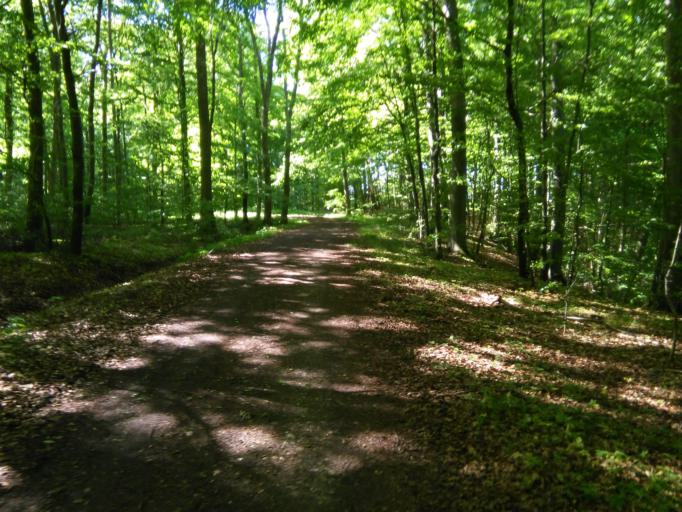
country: DK
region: Central Jutland
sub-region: Arhus Kommune
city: Malling
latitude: 56.0250
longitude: 10.1598
